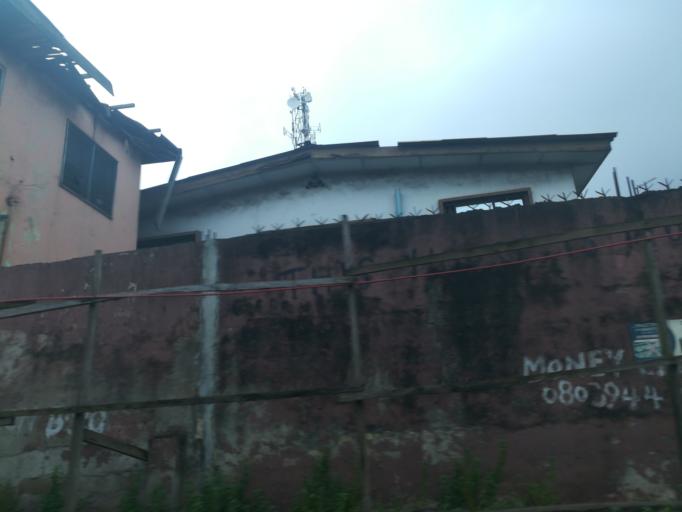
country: NG
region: Lagos
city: Ikeja
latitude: 6.5999
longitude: 3.3347
